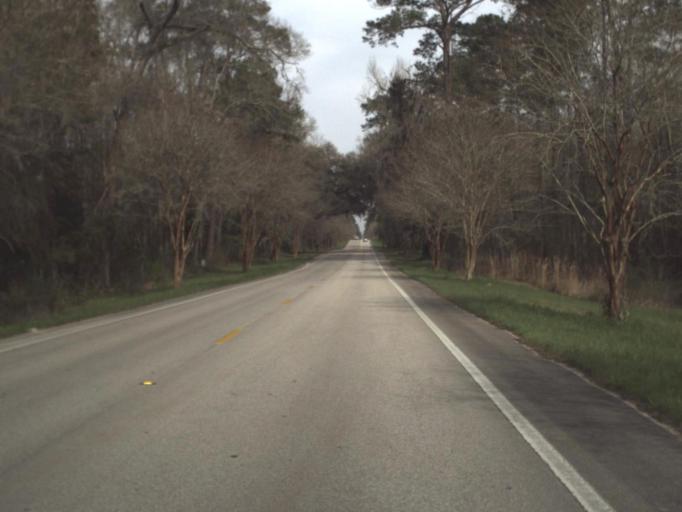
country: US
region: Florida
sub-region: Jefferson County
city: Monticello
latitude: 30.5334
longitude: -83.9501
